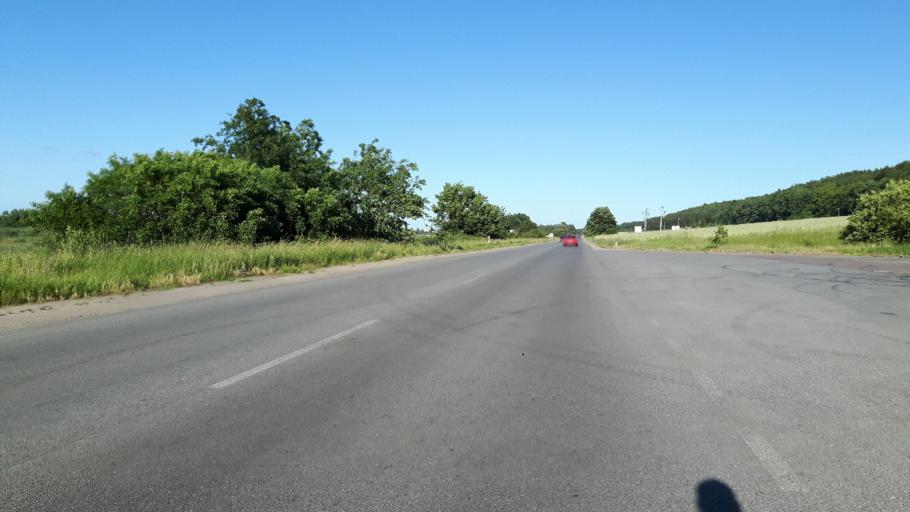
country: PL
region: Pomeranian Voivodeship
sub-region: Powiat pucki
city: Mrzezino
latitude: 54.6051
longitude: 18.4295
